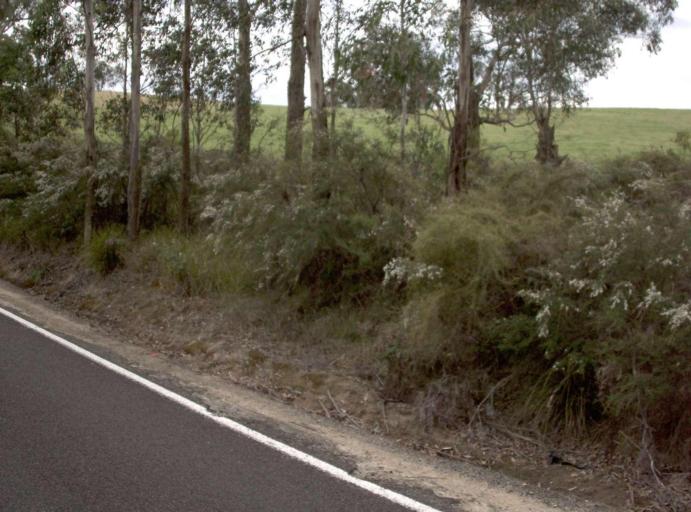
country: AU
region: New South Wales
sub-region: Bombala
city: Bombala
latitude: -37.4757
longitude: 149.1801
